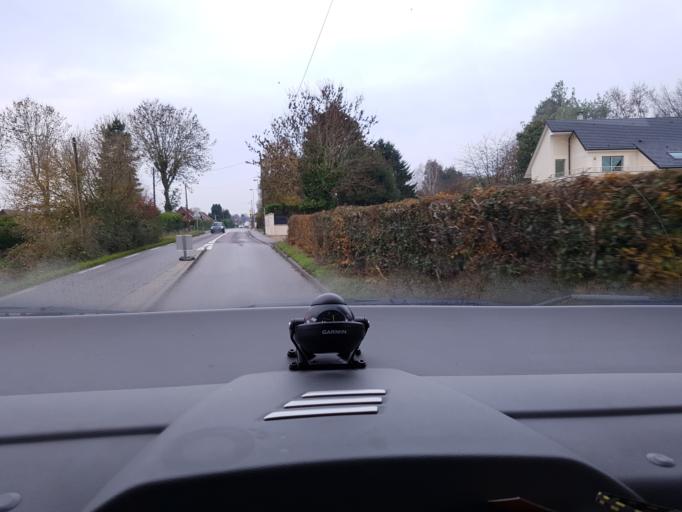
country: FR
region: Haute-Normandie
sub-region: Departement de la Seine-Maritime
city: Roumare
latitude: 49.4997
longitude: 0.9736
